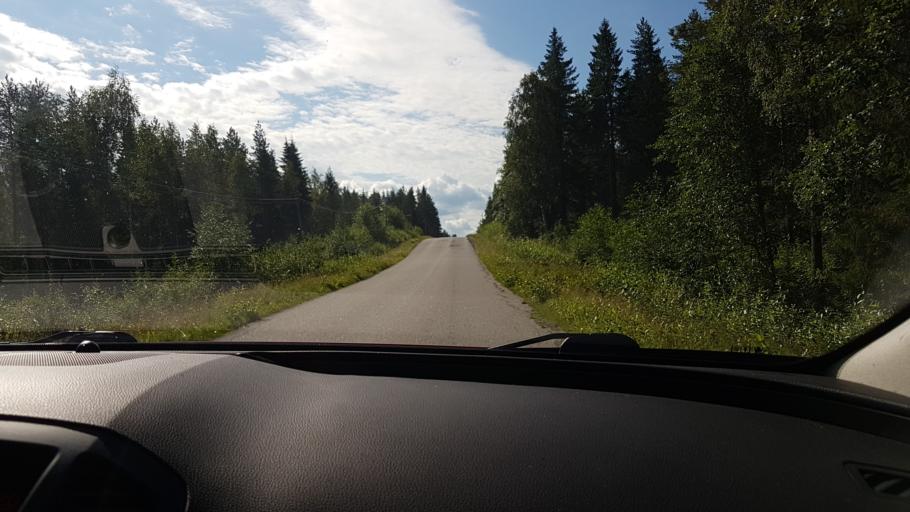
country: FI
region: Central Ostrobothnia
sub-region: Kokkola
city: Kannus
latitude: 64.0356
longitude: 23.8922
